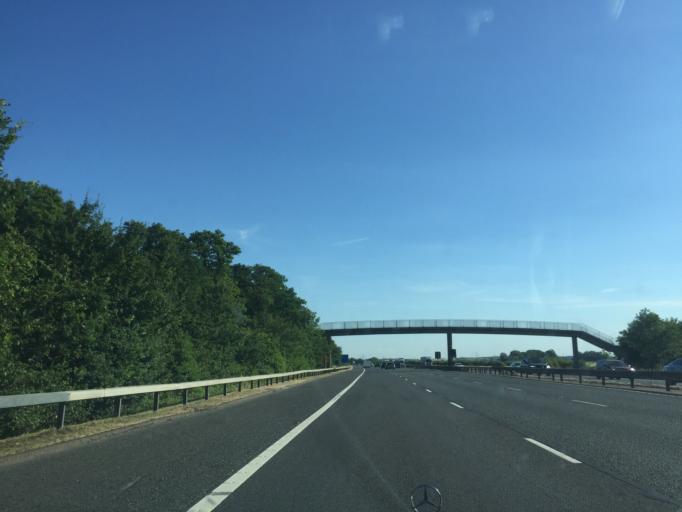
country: GB
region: England
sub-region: Oxfordshire
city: Wheatley
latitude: 51.7761
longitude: -1.0982
